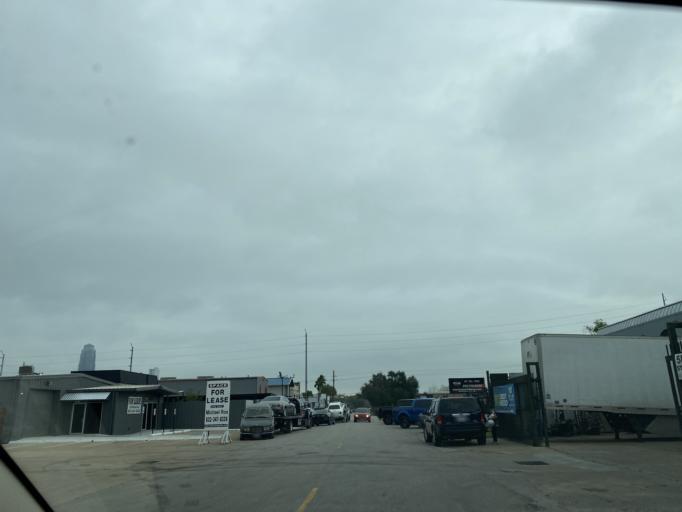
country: US
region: Texas
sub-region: Harris County
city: Bellaire
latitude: 29.7275
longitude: -95.4823
